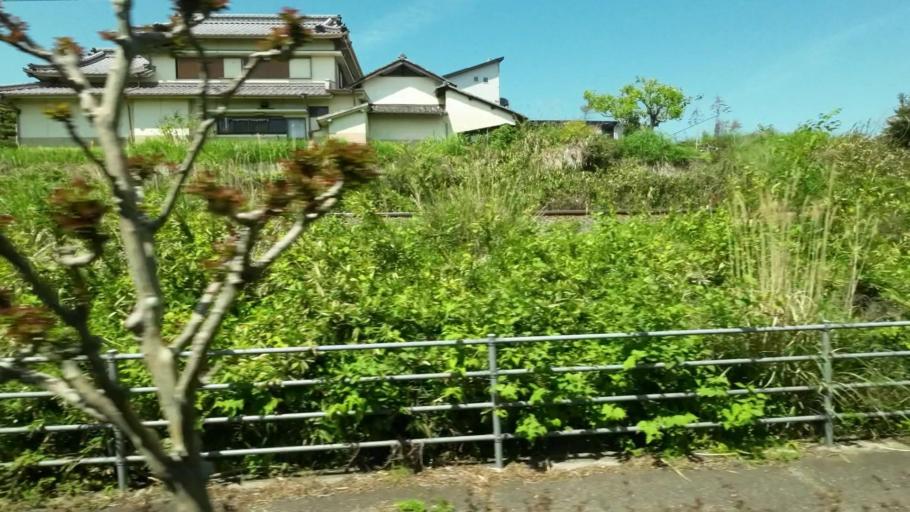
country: JP
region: Ehime
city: Hojo
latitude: 34.0838
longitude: 132.9844
